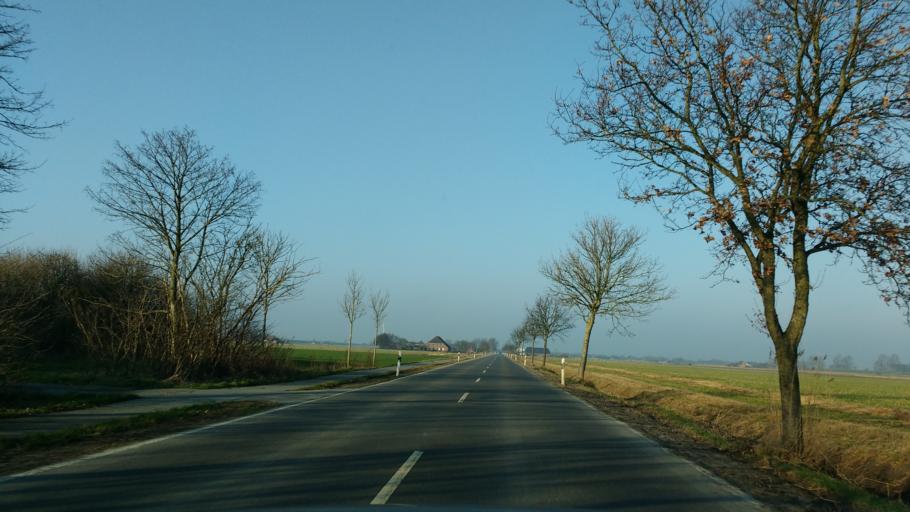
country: DE
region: Schleswig-Holstein
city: Friedrichskoog
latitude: 53.9888
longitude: 8.9084
